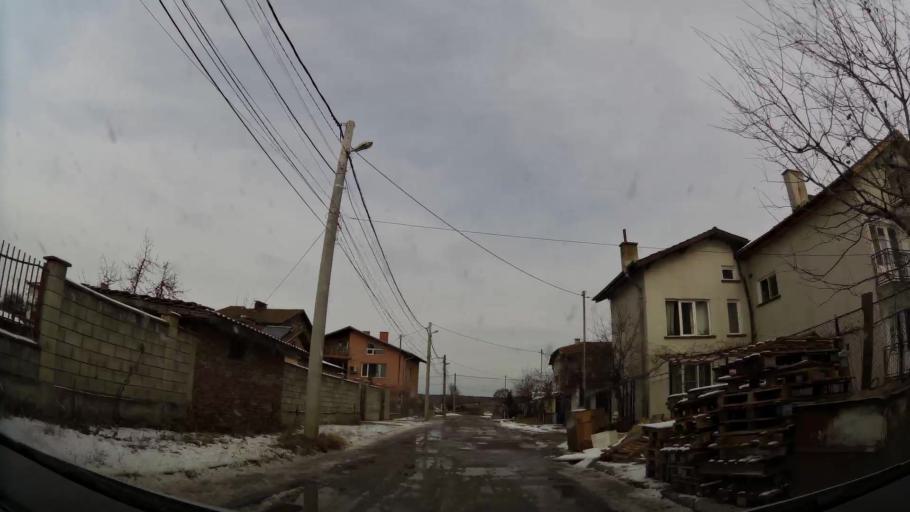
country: BG
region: Sofia-Capital
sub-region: Stolichna Obshtina
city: Sofia
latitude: 42.7159
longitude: 23.4098
